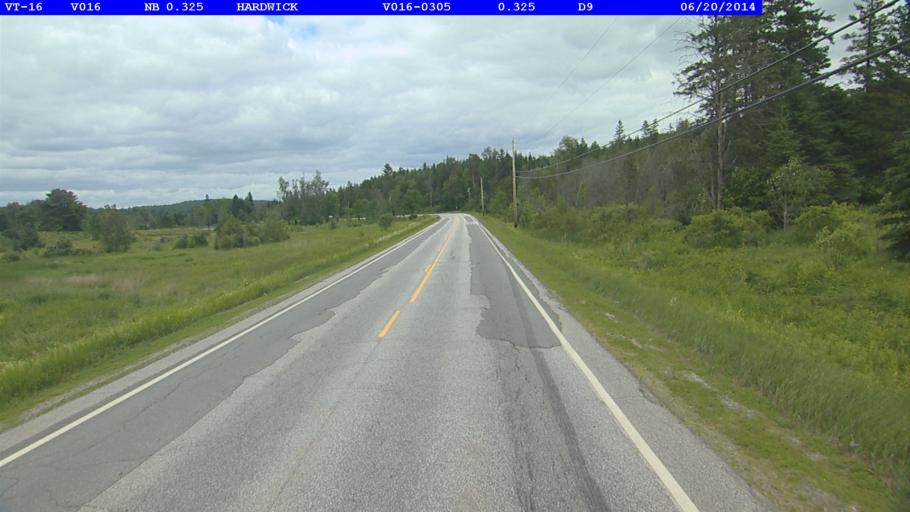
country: US
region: Vermont
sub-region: Caledonia County
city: Hardwick
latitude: 44.5028
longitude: -72.3192
